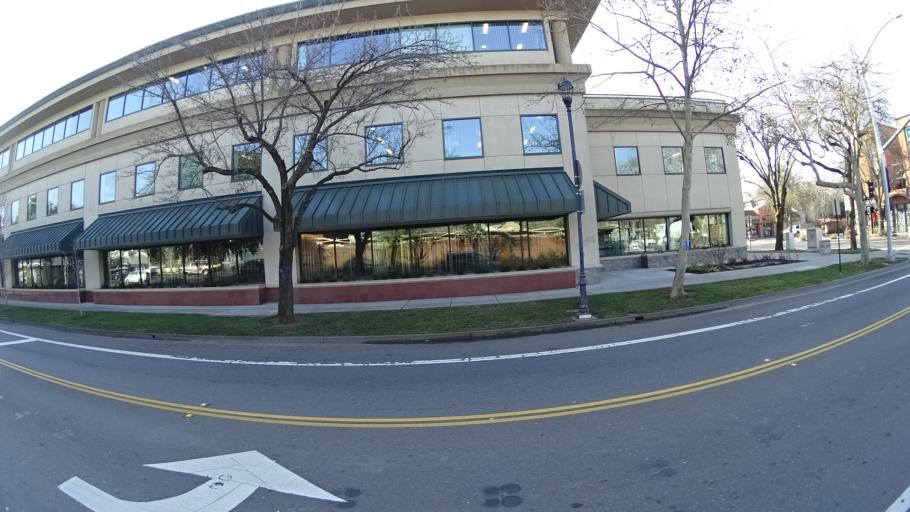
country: US
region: California
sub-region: Yolo County
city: Davis
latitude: 38.5476
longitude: -121.7396
